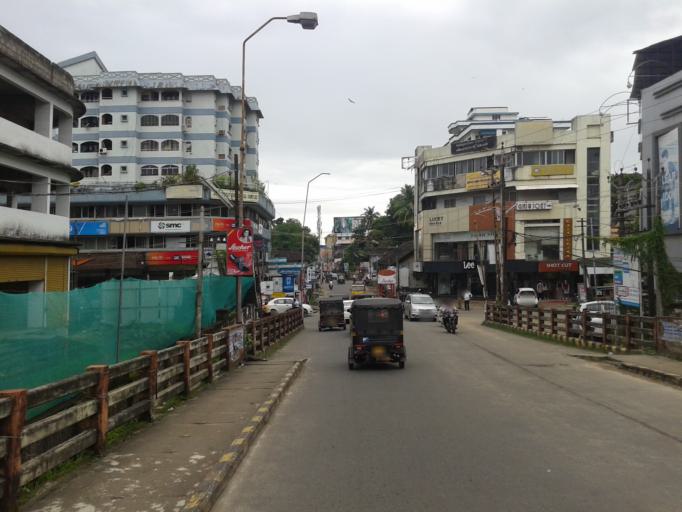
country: IN
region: Kerala
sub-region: Kozhikode
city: Kozhikode
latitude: 11.2564
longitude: 75.7765
